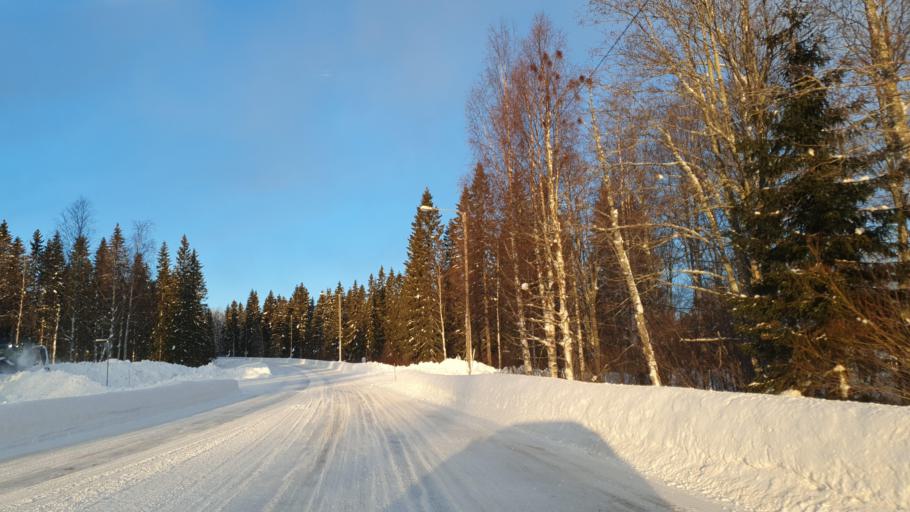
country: FI
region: Kainuu
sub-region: Kajaani
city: Ristijaervi
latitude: 64.3392
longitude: 28.1040
